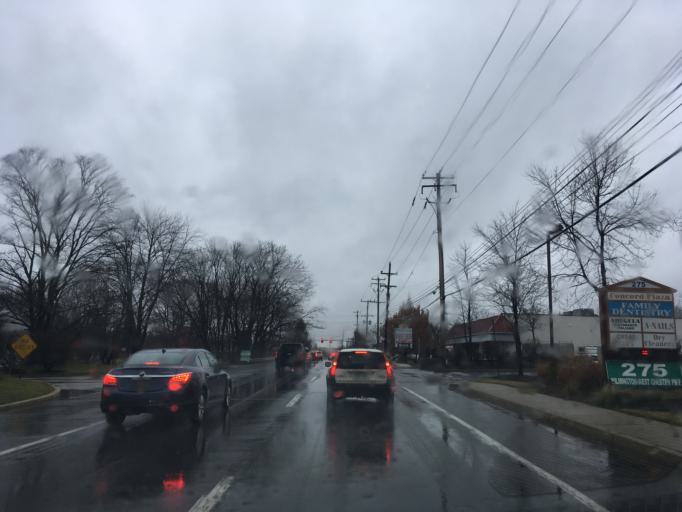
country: US
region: Pennsylvania
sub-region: Delaware County
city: Chester Heights
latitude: 39.8539
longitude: -75.5395
